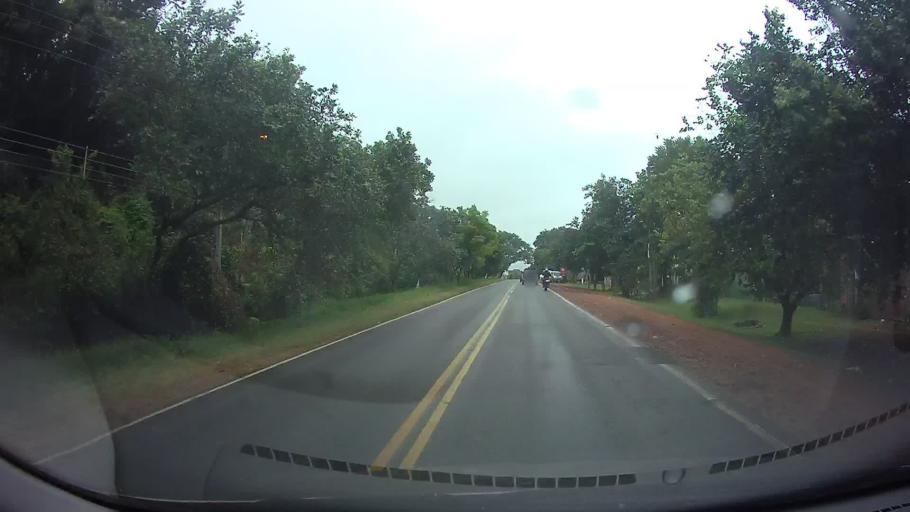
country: PY
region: Central
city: Itaugua
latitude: -25.4045
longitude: -57.3588
